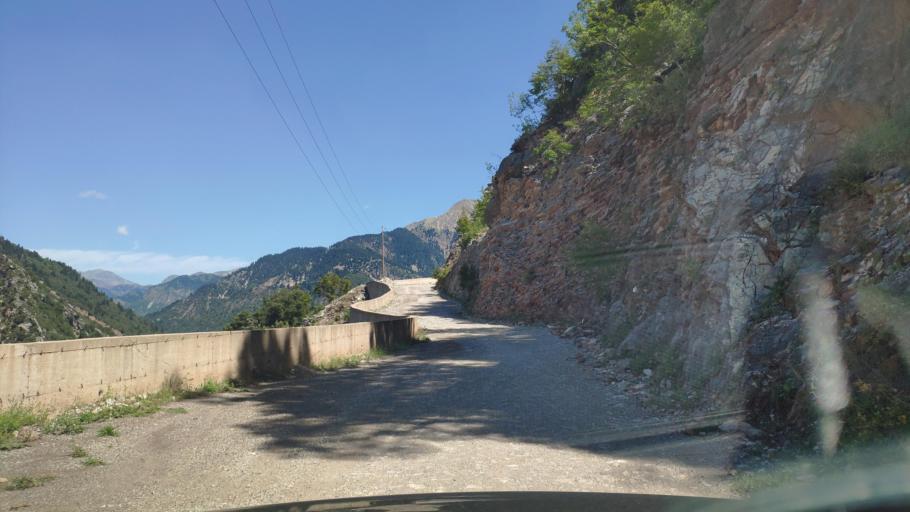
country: GR
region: Central Greece
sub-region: Nomos Evrytanias
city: Kerasochori
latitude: 39.1141
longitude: 21.6180
